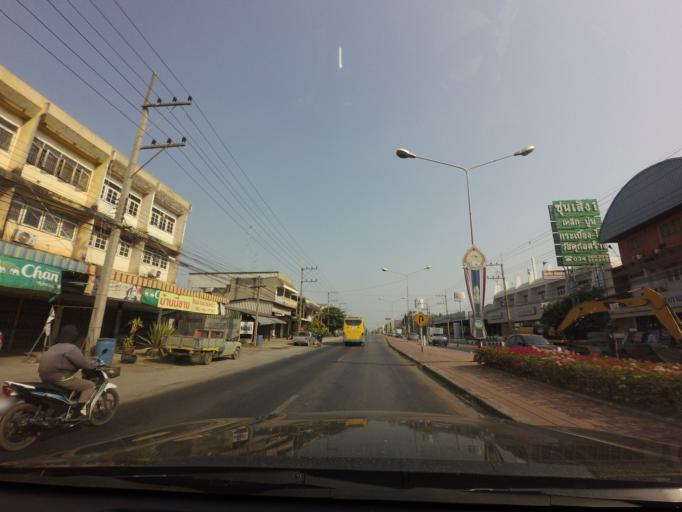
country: TH
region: Kanchanaburi
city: Tha Maka
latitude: 13.8783
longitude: 99.8094
